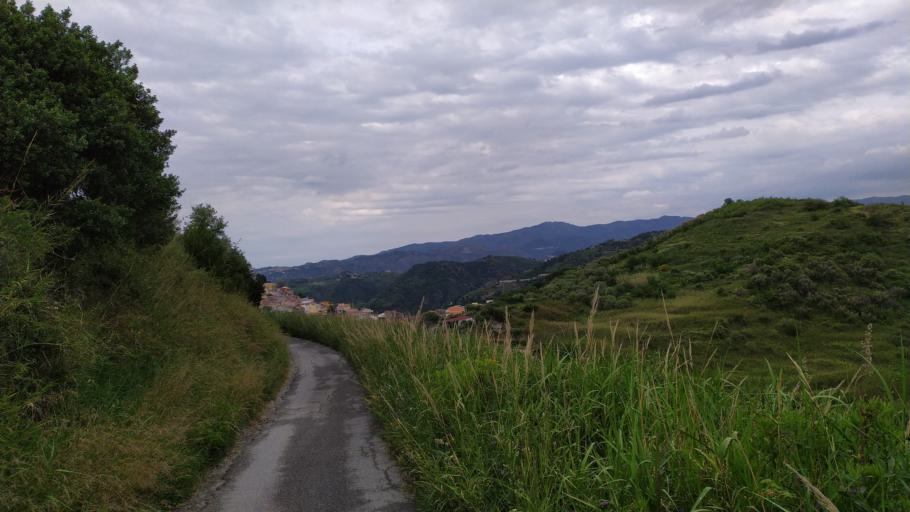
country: IT
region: Sicily
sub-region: Messina
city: Gualtieri Sicamino
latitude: 38.1586
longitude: 15.3016
